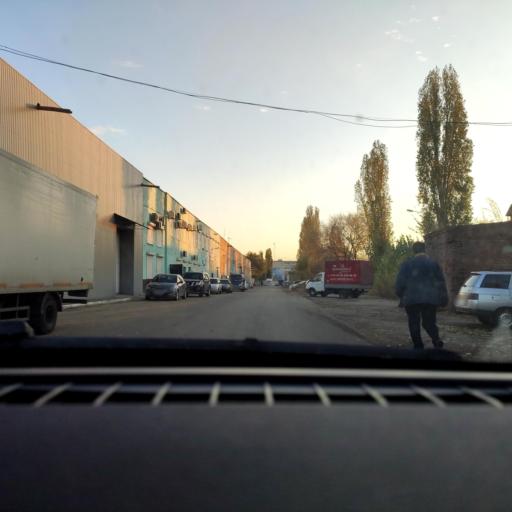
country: RU
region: Voronezj
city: Maslovka
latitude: 51.6389
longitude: 39.2842
